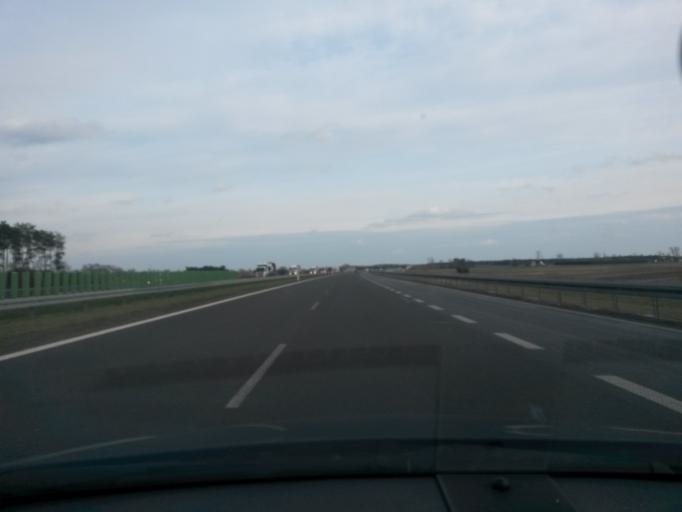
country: PL
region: Greater Poland Voivodeship
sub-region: Powiat kolski
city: Dabie
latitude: 52.0963
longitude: 18.7744
